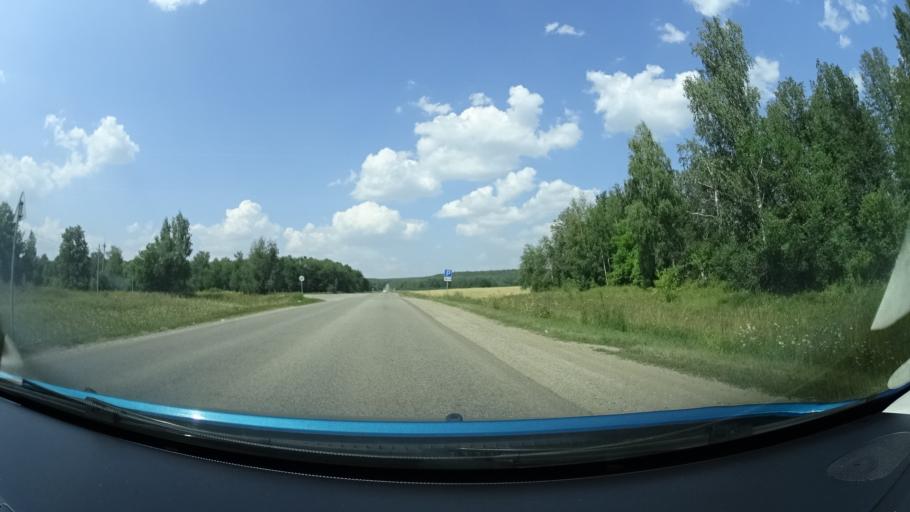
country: RU
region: Bashkortostan
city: Oktyabr'skiy
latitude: 54.4501
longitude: 53.5972
